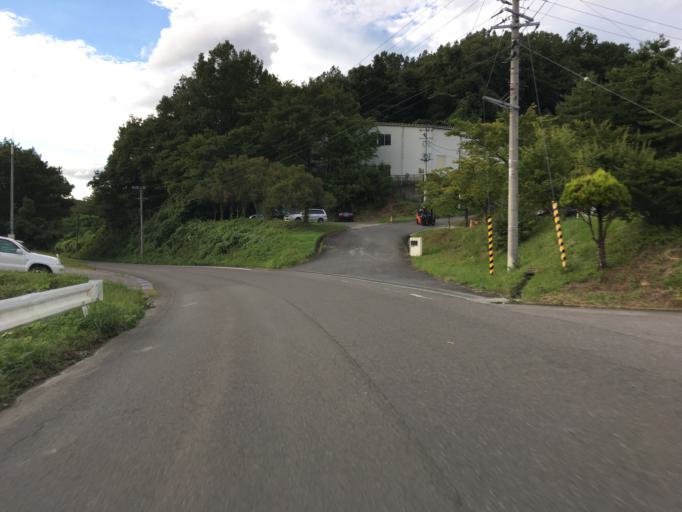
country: JP
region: Fukushima
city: Nihommatsu
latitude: 37.6318
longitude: 140.4970
